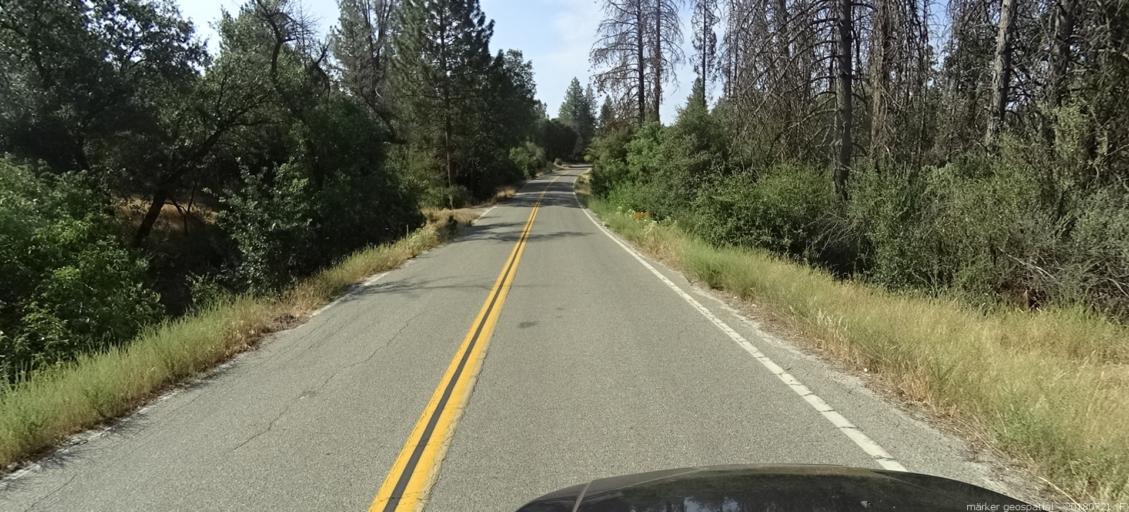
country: US
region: California
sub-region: Fresno County
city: Auberry
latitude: 37.2251
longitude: -119.5278
